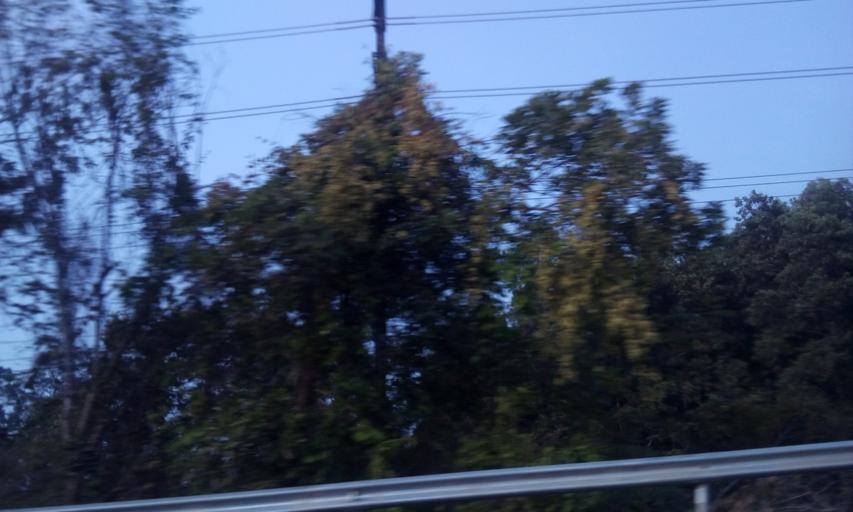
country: TH
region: Chanthaburi
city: Khlung
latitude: 12.4448
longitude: 102.2953
